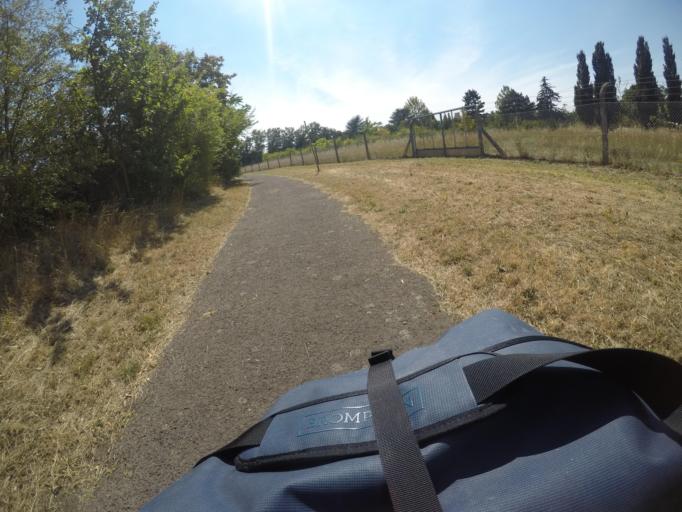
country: DE
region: Hesse
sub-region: Regierungsbezirk Darmstadt
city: Hochheim am Main
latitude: 49.9966
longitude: 8.3425
